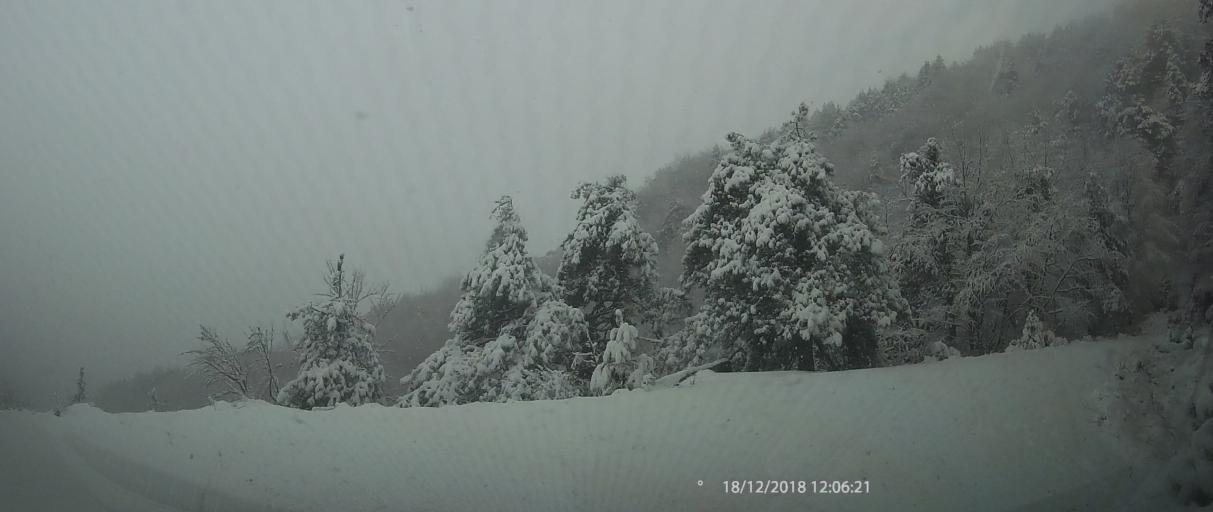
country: GR
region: Central Macedonia
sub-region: Nomos Pierias
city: Litochoro
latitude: 40.1052
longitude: 22.4578
